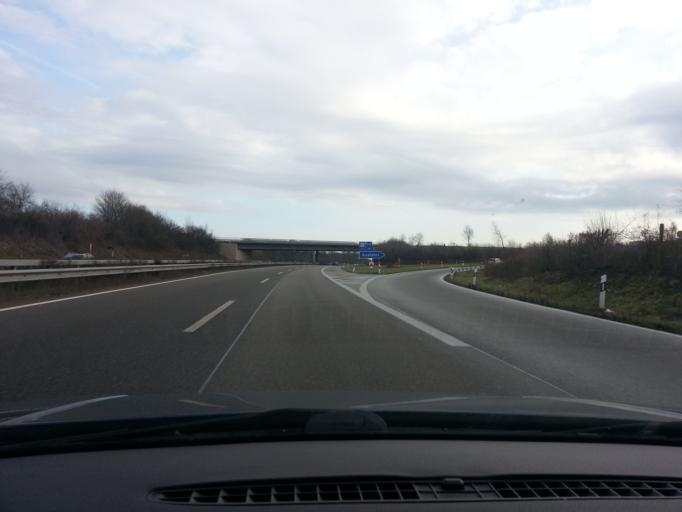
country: DE
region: Rheinland-Pfalz
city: Zweibrucken
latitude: 49.2368
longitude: 7.3947
